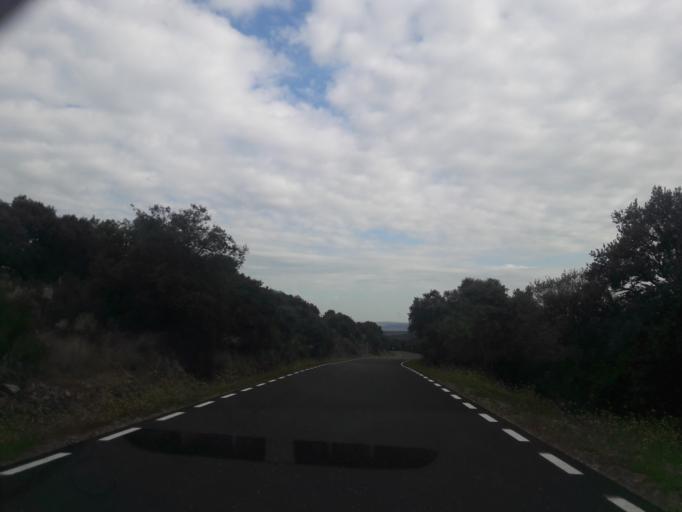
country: ES
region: Castille and Leon
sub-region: Provincia de Salamanca
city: Pastores
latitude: 40.5199
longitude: -6.5264
